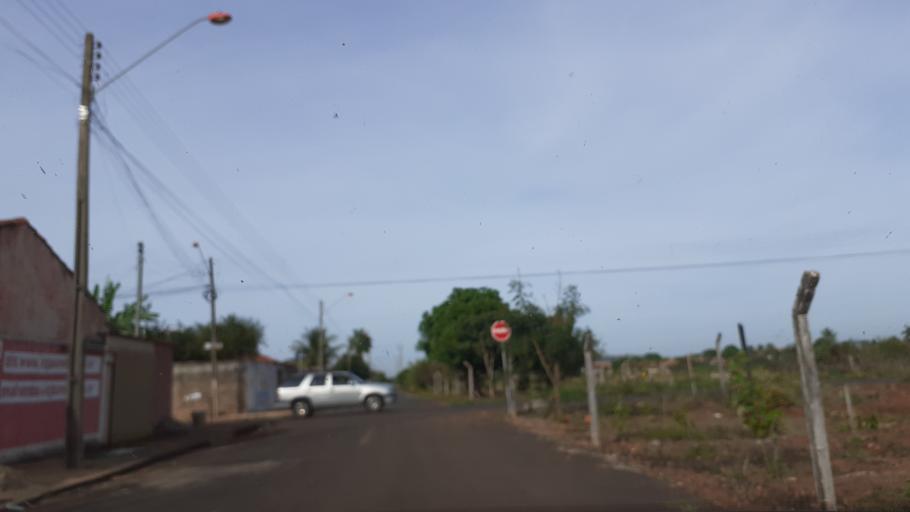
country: BR
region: Goias
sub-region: Itumbiara
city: Itumbiara
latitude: -18.4162
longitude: -49.2467
